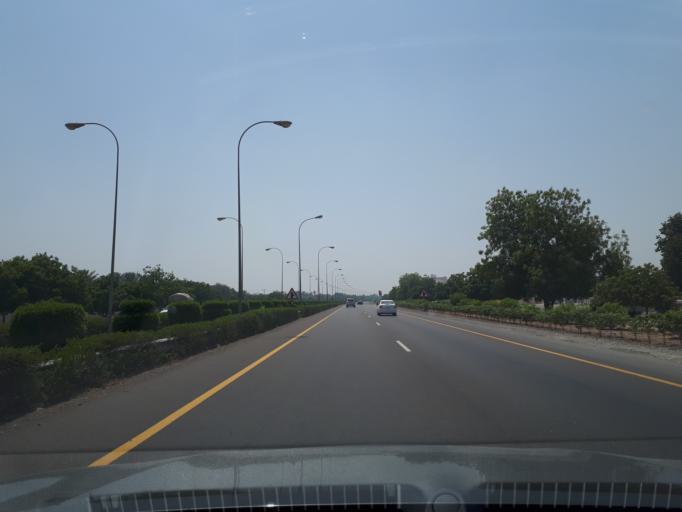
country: OM
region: Al Batinah
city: Al Sohar
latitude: 24.3949
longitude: 56.6810
